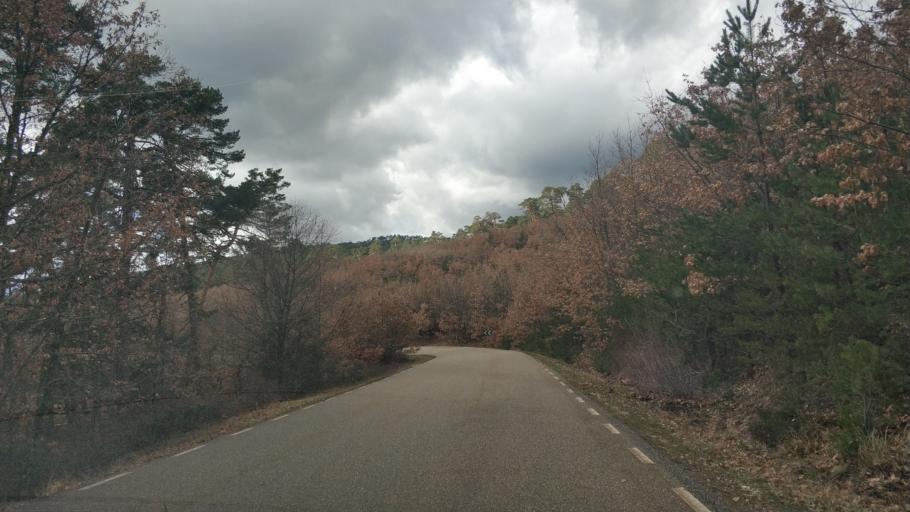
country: ES
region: Castille and Leon
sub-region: Provincia de Burgos
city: Quintanar de la Sierra
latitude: 41.9976
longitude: -3.0177
